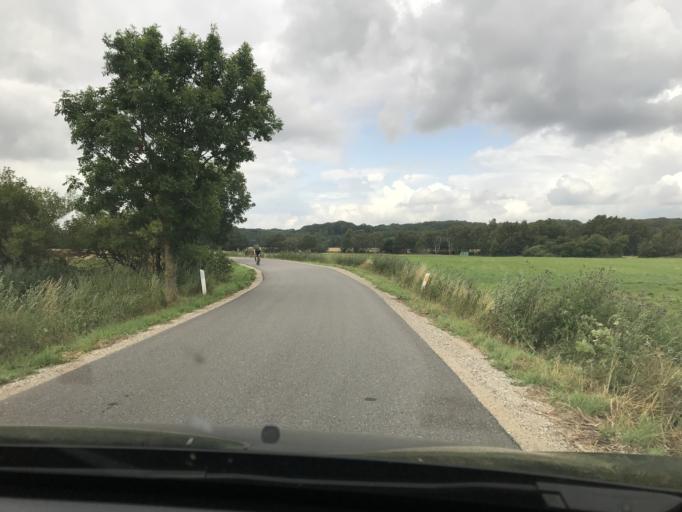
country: DK
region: Central Jutland
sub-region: Syddjurs Kommune
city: Ryomgard
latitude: 56.3791
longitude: 10.4320
